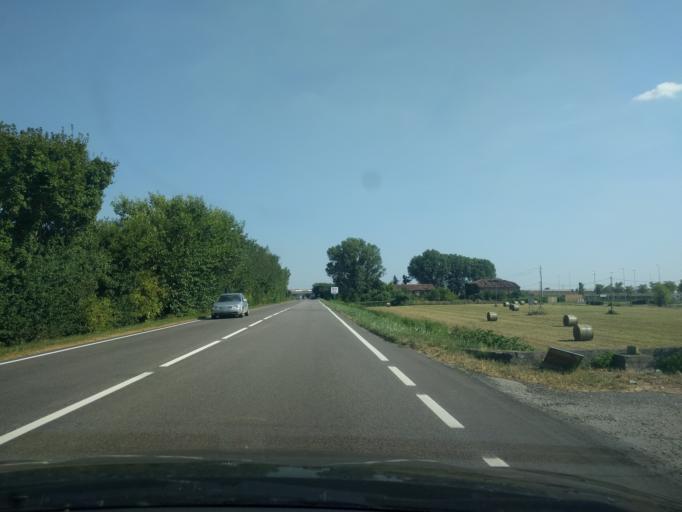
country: IT
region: Veneto
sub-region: Provincia di Padova
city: Stanghella
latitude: 45.1235
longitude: 11.7666
